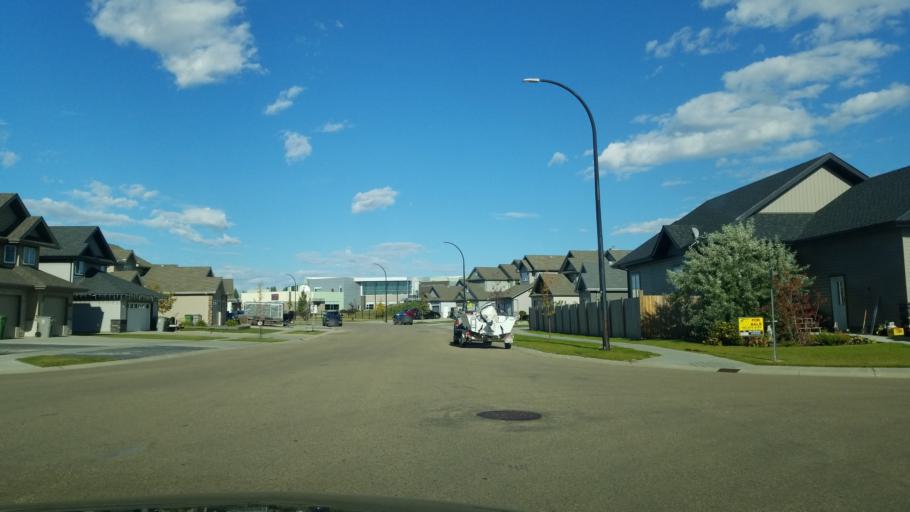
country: CA
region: Saskatchewan
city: Lloydminster
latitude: 53.2547
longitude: -110.0229
